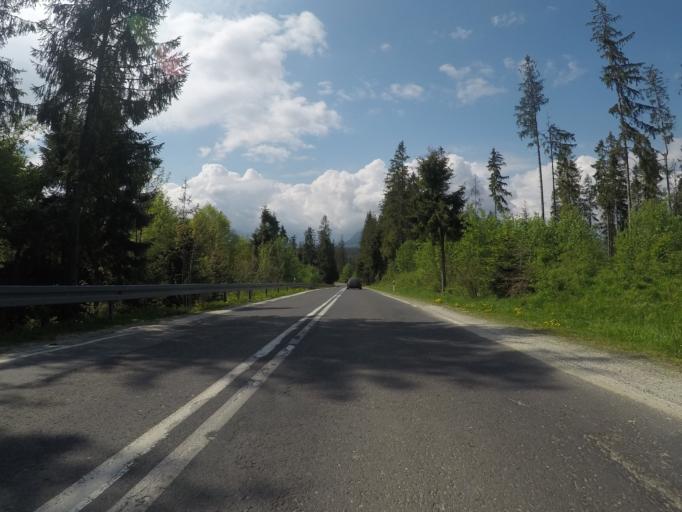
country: PL
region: Lesser Poland Voivodeship
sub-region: Powiat tatrzanski
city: Bukowina Tatrzanska
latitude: 49.2968
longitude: 20.1151
